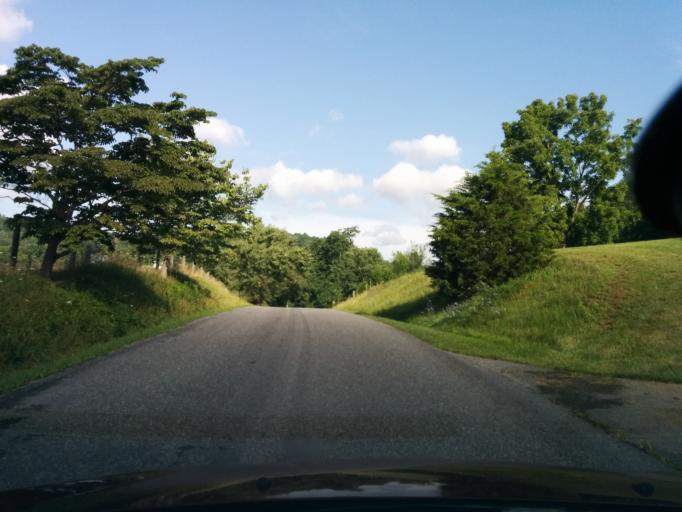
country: US
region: Virginia
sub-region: City of Lexington
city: Lexington
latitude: 37.7751
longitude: -79.4909
